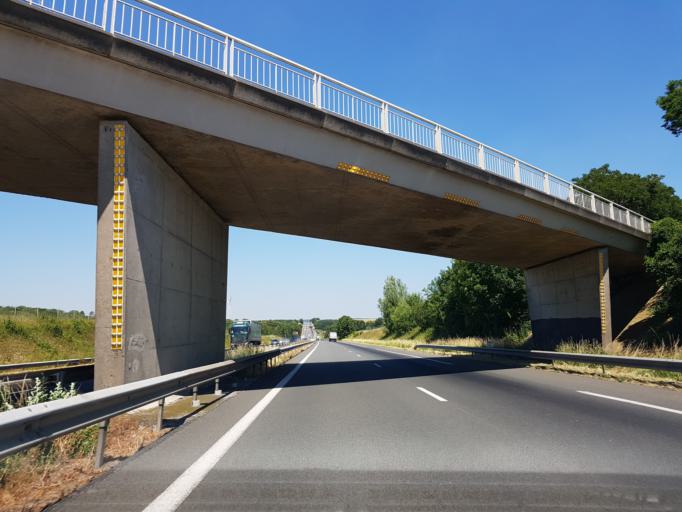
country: FR
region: Nord-Pas-de-Calais
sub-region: Departement du Nord
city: Marcoing
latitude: 50.1065
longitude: 3.1641
